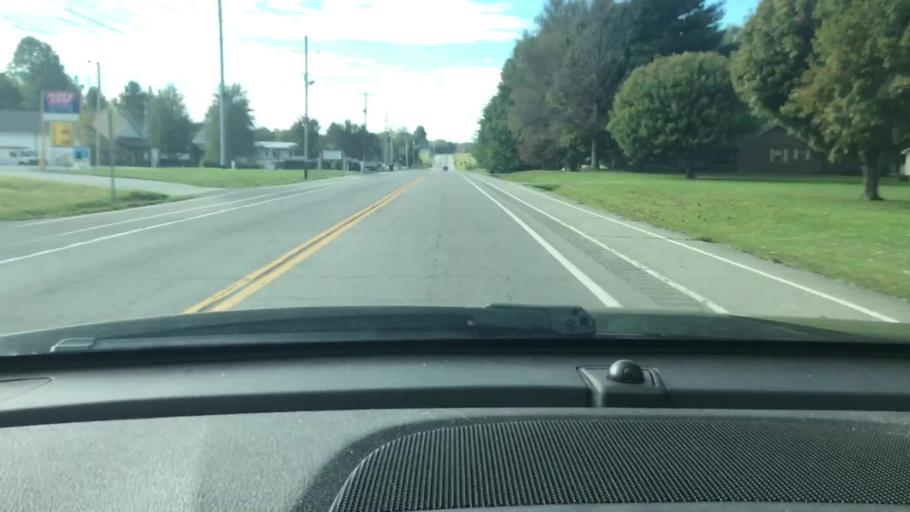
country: US
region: Tennessee
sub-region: Sumner County
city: White House
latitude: 36.4475
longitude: -86.6770
